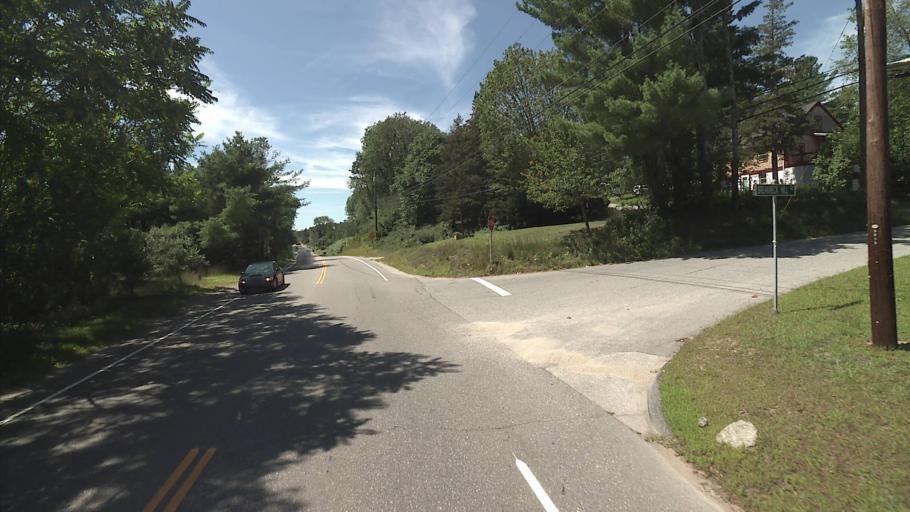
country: US
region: Connecticut
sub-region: Windham County
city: Killingly Center
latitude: 41.8402
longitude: -71.8606
